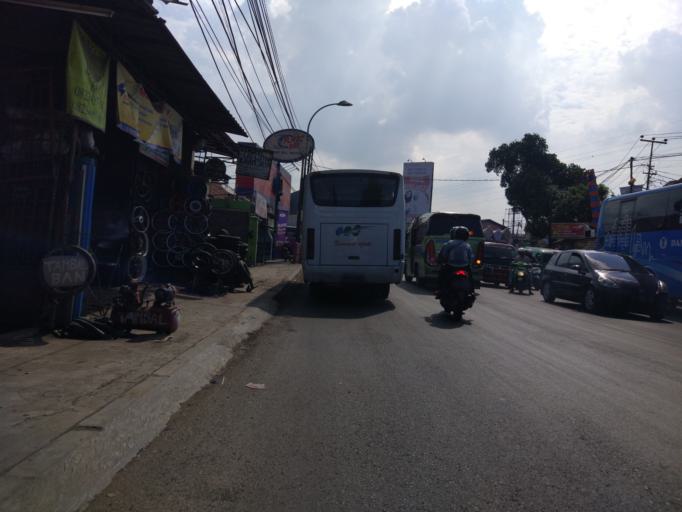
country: ID
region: West Java
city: Cileunyi
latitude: -6.9363
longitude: 107.7289
